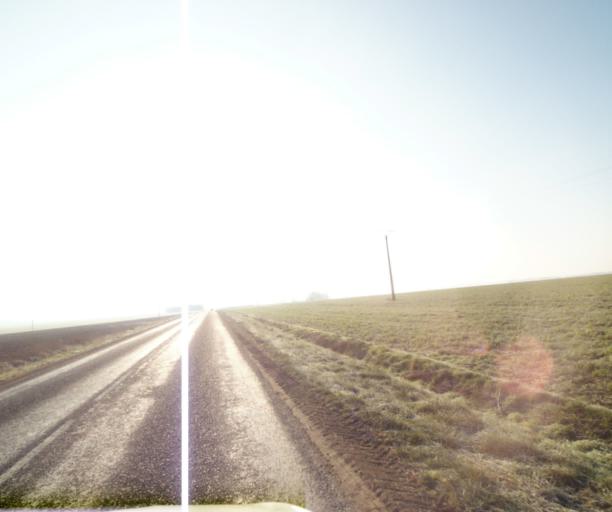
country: FR
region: Champagne-Ardenne
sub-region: Departement de la Haute-Marne
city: Montier-en-Der
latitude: 48.4984
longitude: 4.7522
